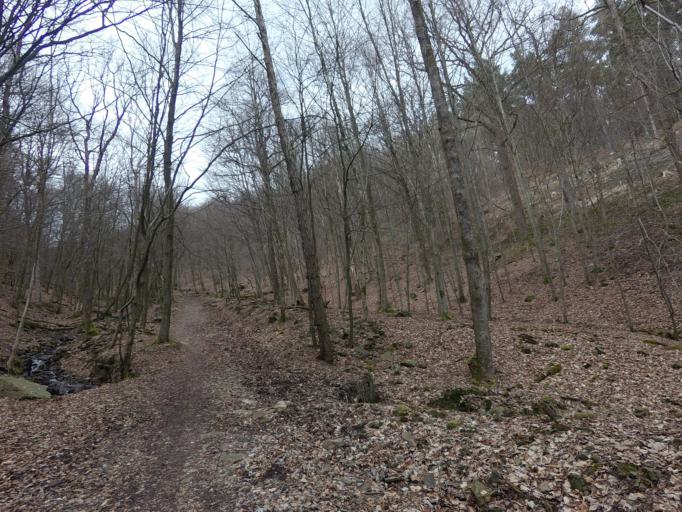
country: BE
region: Wallonia
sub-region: Province de Liege
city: Aywaille
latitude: 50.4075
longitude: 5.7218
